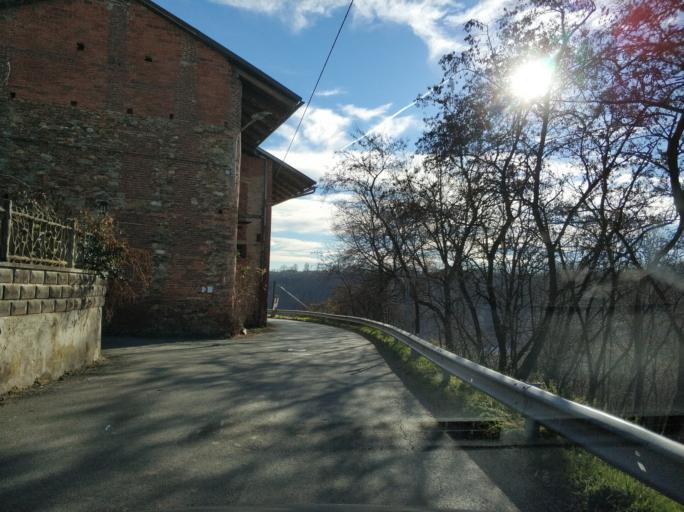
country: IT
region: Piedmont
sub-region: Provincia di Torino
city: Vauda Canavese Superiore
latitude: 45.2865
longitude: 7.6058
